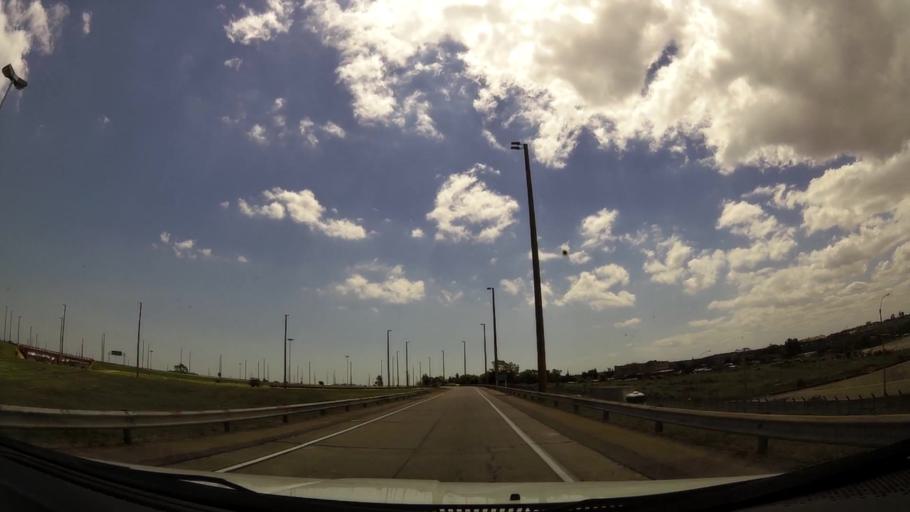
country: UY
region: Canelones
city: La Paz
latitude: -34.8238
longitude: -56.2459
